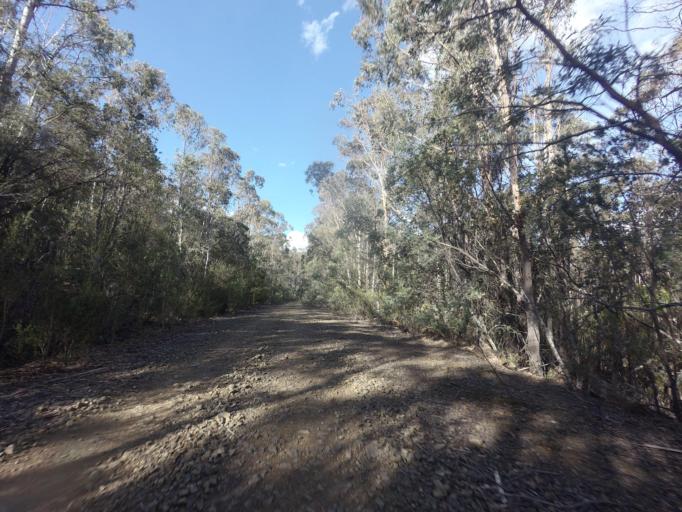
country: AU
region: Tasmania
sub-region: Break O'Day
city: St Helens
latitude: -41.8460
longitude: 148.0585
